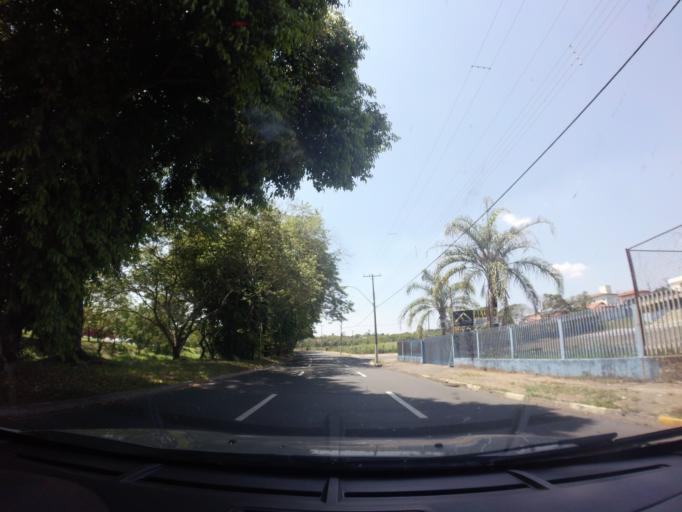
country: BR
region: Sao Paulo
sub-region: Piracicaba
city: Piracicaba
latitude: -22.7240
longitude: -47.6252
